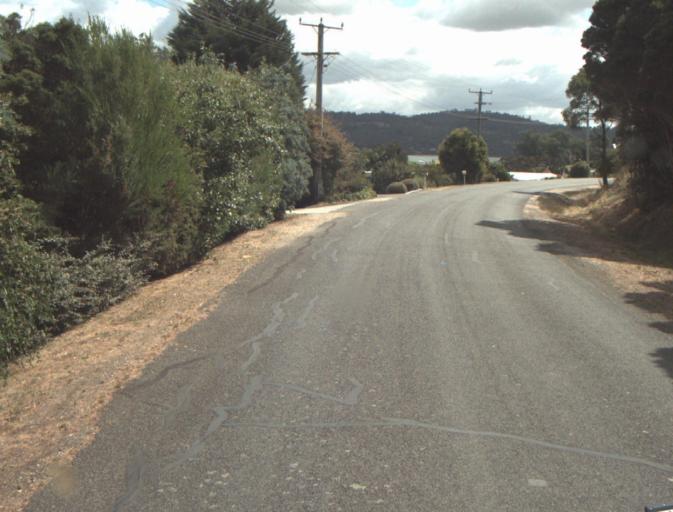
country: AU
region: Tasmania
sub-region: Launceston
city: Mayfield
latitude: -41.3152
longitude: 147.0184
